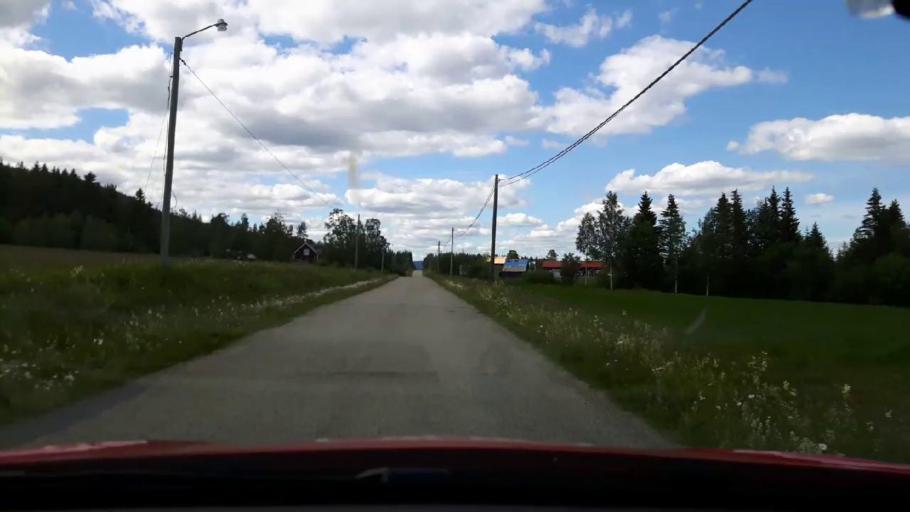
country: SE
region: Jaemtland
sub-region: Bergs Kommun
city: Hoverberg
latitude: 62.8350
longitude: 14.4529
